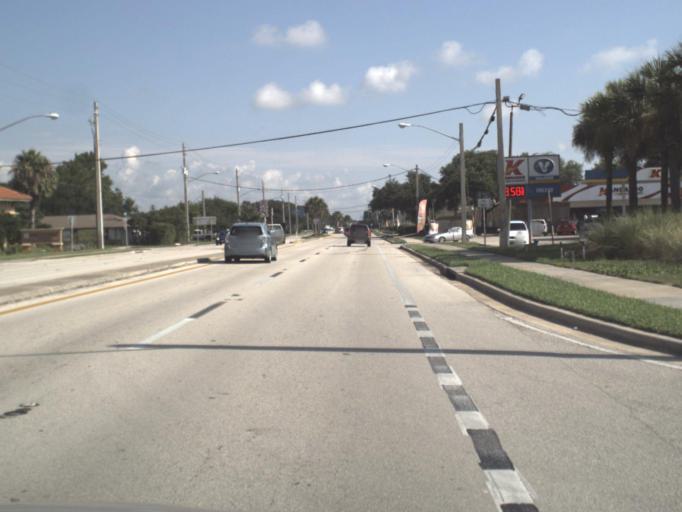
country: US
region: Florida
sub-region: Saint Johns County
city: Saint Augustine Beach
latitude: 29.8260
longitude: -81.2717
